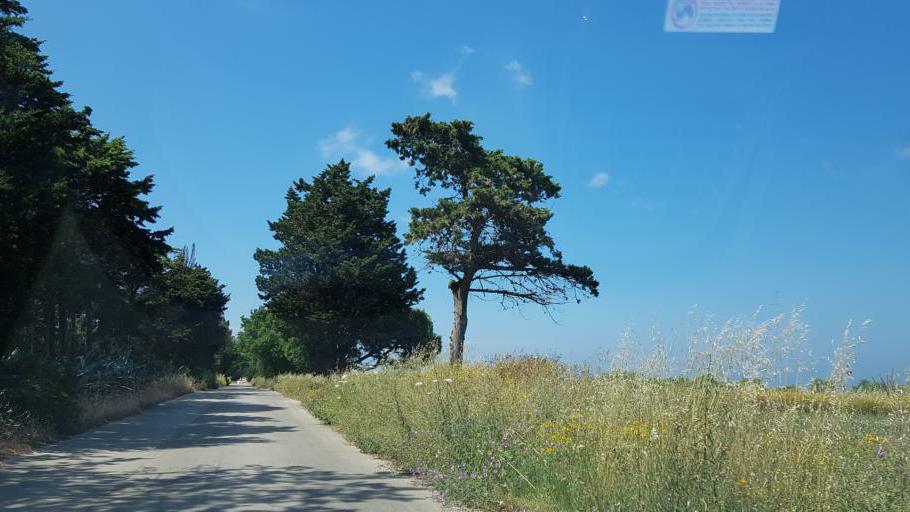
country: IT
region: Apulia
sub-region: Provincia di Brindisi
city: Brindisi
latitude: 40.6500
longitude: 17.8550
